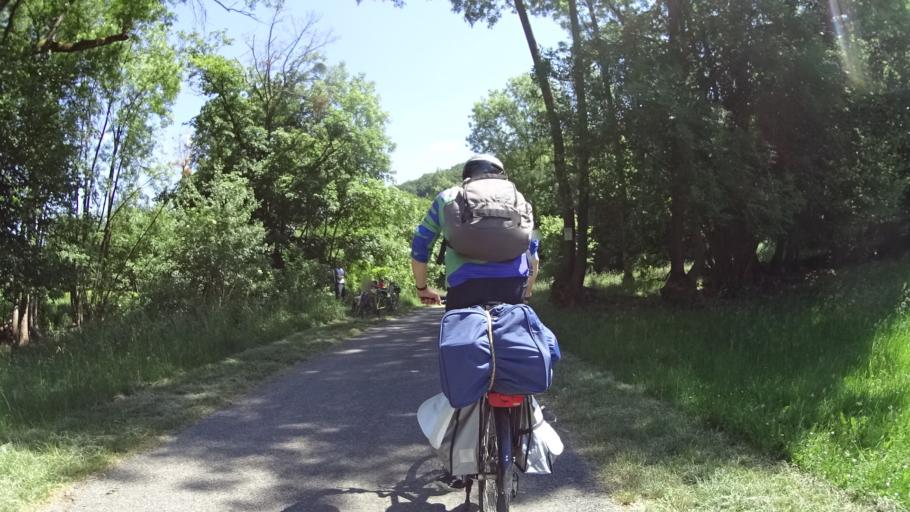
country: DE
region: Bavaria
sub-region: Regierungsbezirk Mittelfranken
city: Adelshofen
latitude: 49.4448
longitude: 10.1059
